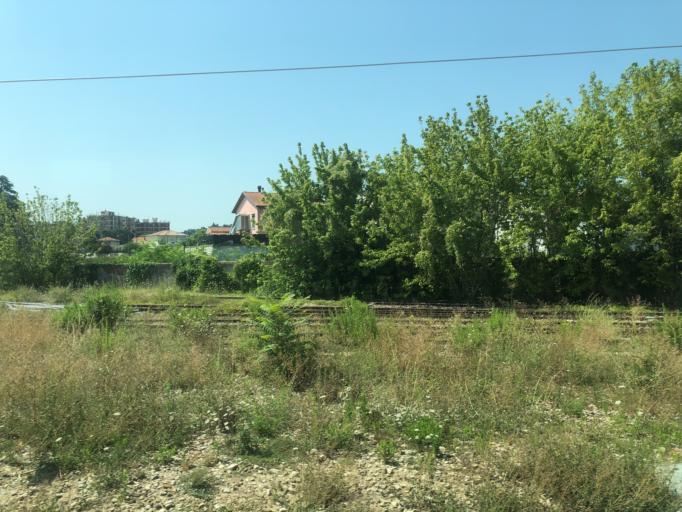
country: IT
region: Emilia-Romagna
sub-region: Forli-Cesena
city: Cesena
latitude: 44.1472
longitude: 12.2441
